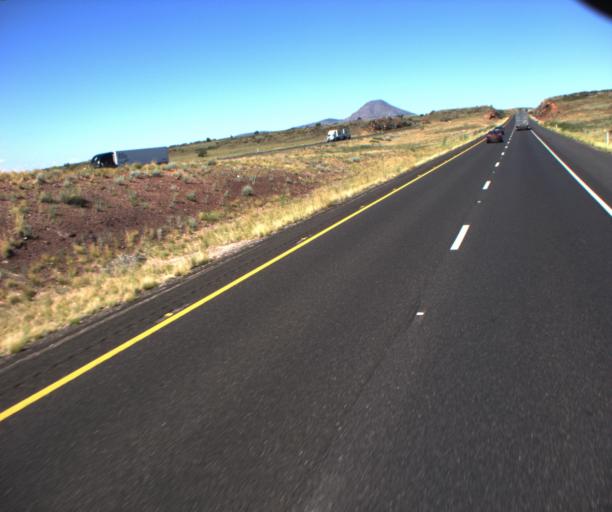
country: US
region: Arizona
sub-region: Yavapai County
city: Paulden
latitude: 35.2362
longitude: -112.6388
